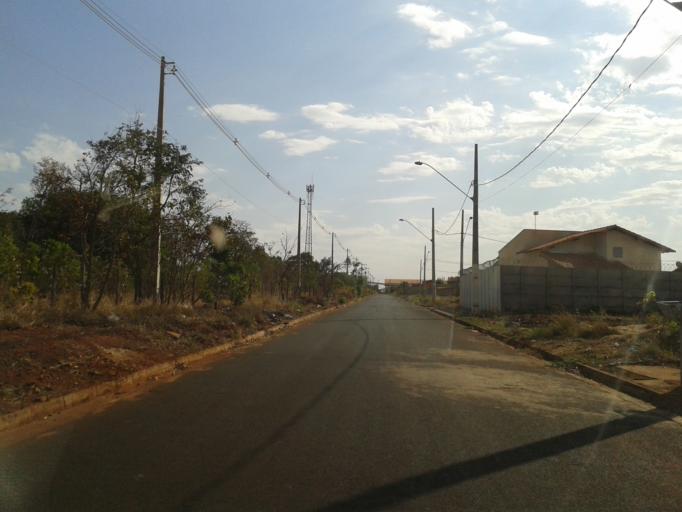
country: BR
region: Minas Gerais
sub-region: Ituiutaba
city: Ituiutaba
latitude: -18.9876
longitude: -49.4260
